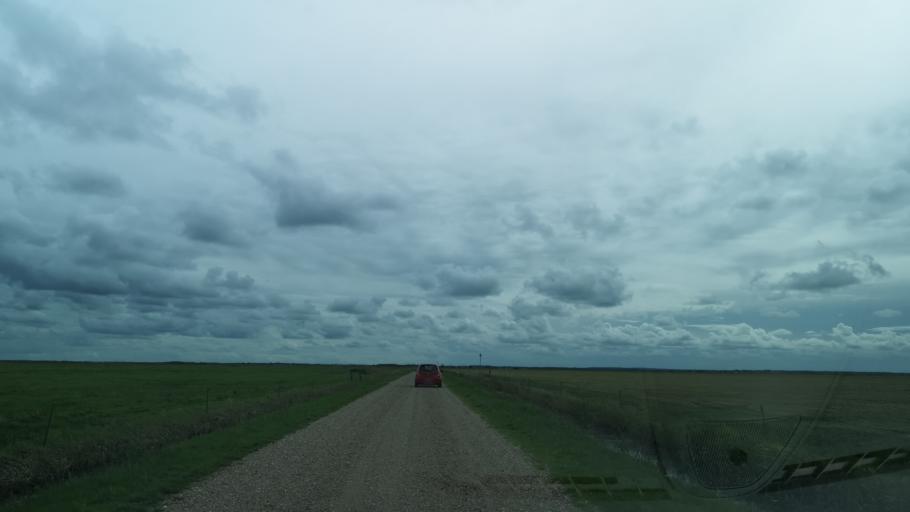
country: DK
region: Central Jutland
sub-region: Ringkobing-Skjern Kommune
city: Hvide Sande
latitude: 55.8825
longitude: 8.2216
